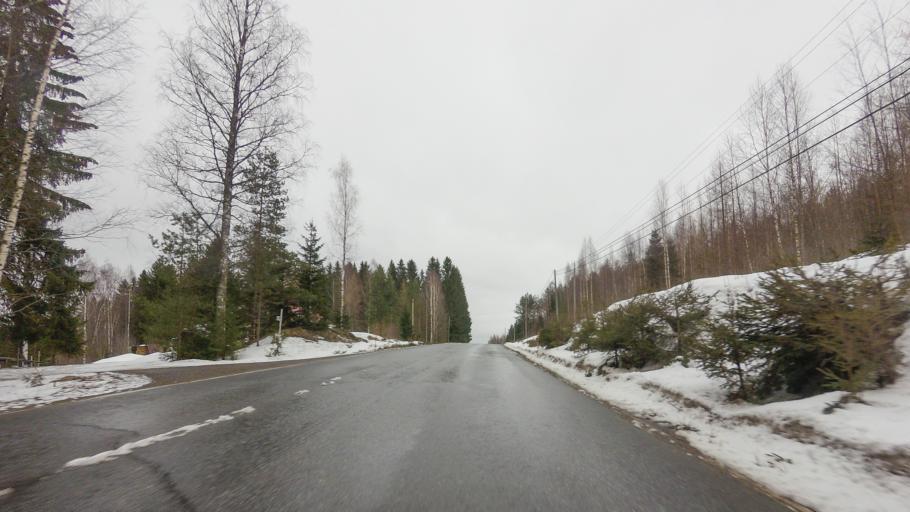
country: FI
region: Southern Savonia
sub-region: Savonlinna
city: Savonlinna
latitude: 61.9494
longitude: 28.8612
